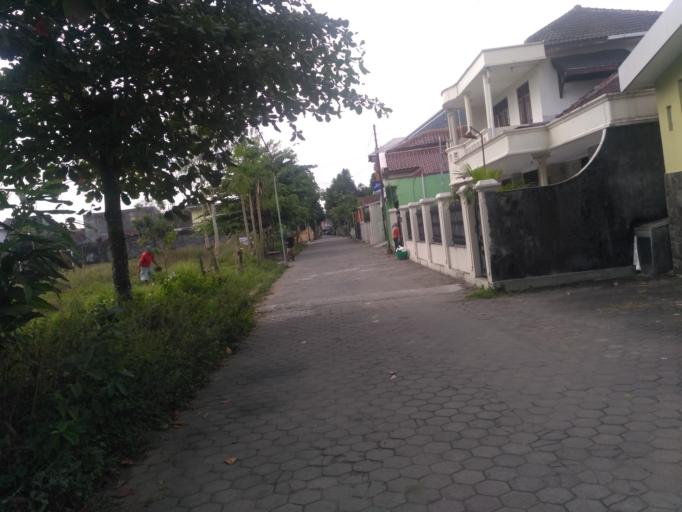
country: ID
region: Daerah Istimewa Yogyakarta
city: Melati
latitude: -7.7519
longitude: 110.3689
